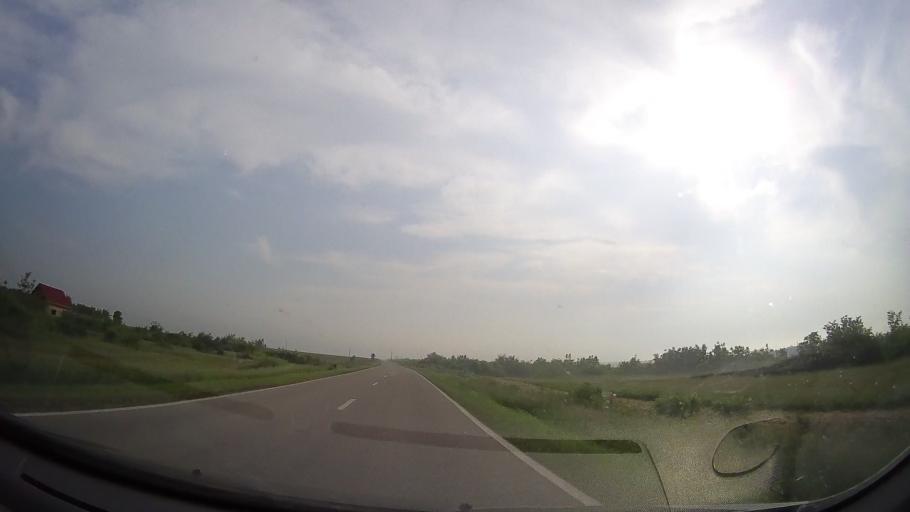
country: RO
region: Timis
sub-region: Comuna Peciu Nou
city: Peciu Nou
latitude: 45.6158
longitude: 21.0758
